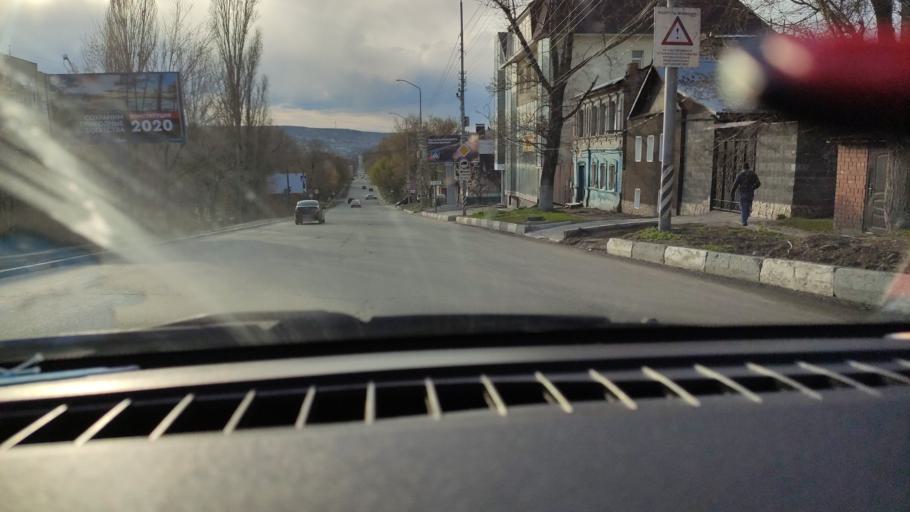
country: RU
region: Saratov
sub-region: Saratovskiy Rayon
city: Saratov
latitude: 51.5415
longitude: 46.0438
